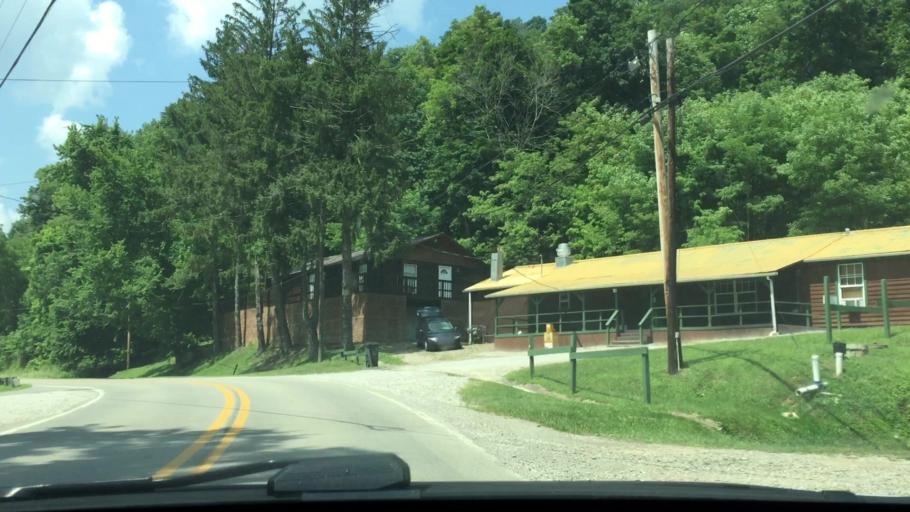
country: US
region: West Virginia
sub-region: Wetzel County
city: New Martinsville
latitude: 39.7062
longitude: -80.8192
